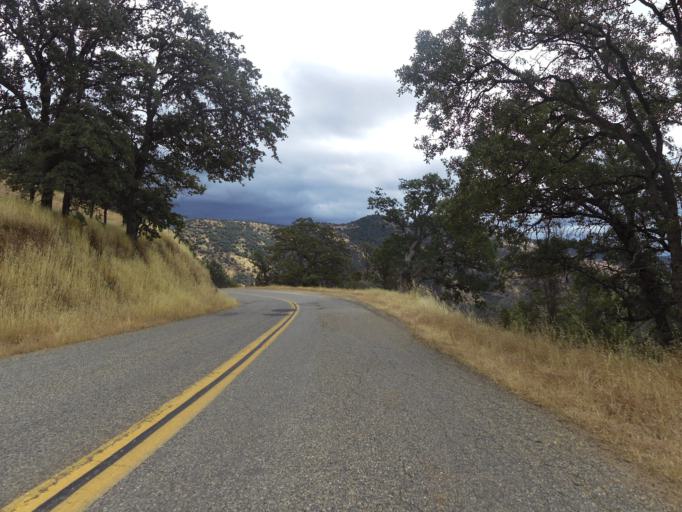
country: US
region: California
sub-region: Madera County
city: Ahwahnee
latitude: 37.3412
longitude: -119.7695
